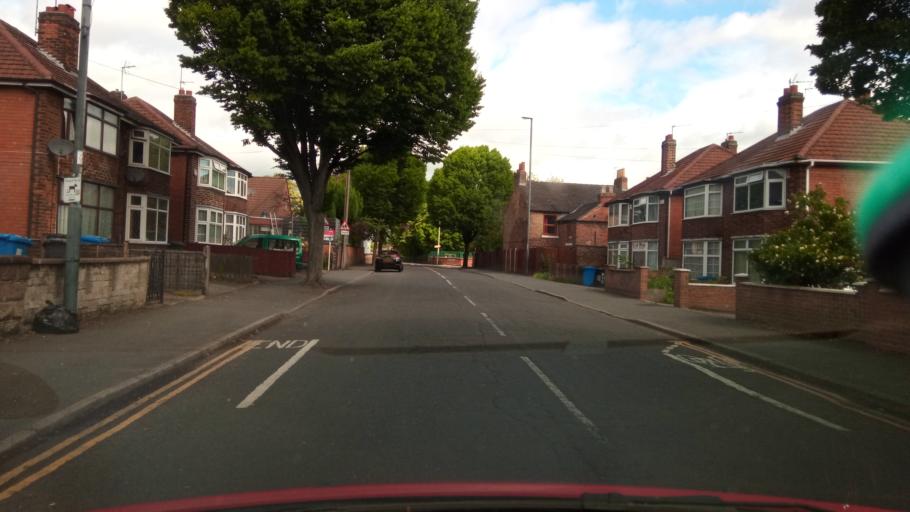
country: GB
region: England
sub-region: Derby
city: Derby
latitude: 52.9007
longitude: -1.4750
